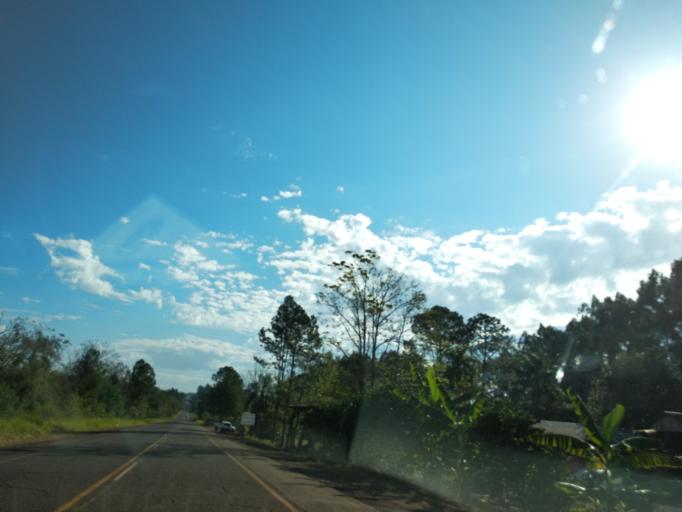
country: AR
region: Misiones
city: Ruiz de Montoya
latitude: -27.0589
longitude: -55.0066
